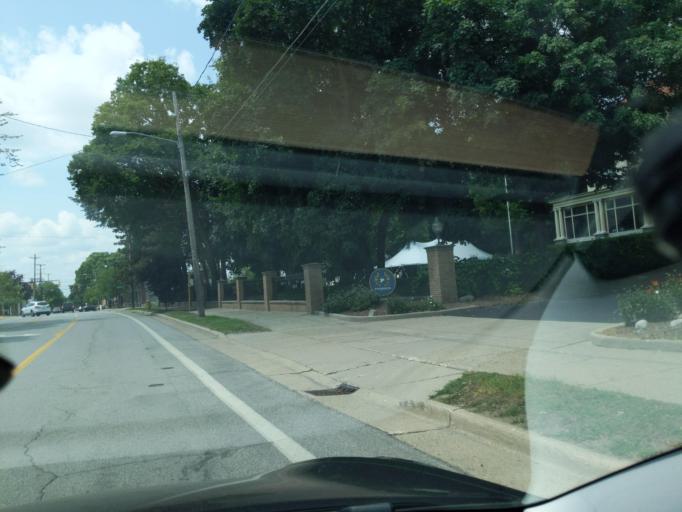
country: US
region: Michigan
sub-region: Kent County
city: Grand Rapids
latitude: 42.9594
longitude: -85.6428
